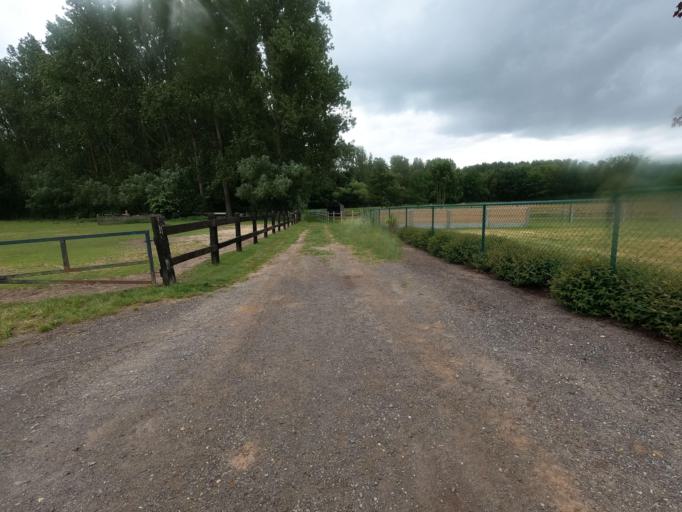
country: BE
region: Flanders
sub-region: Provincie Vlaams-Brabant
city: Tremelo
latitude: 50.9867
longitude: 4.7157
